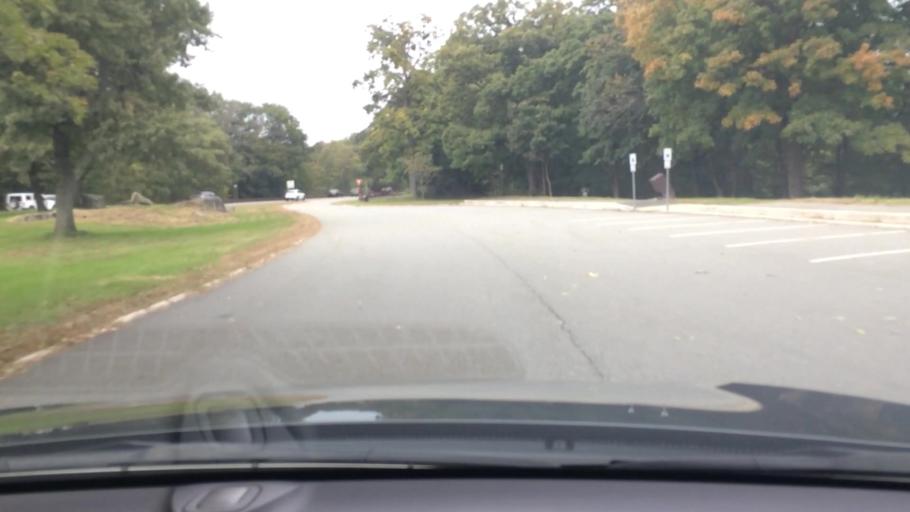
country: US
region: New Jersey
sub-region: Bergen County
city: Alpine
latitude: 40.9311
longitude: -73.9269
